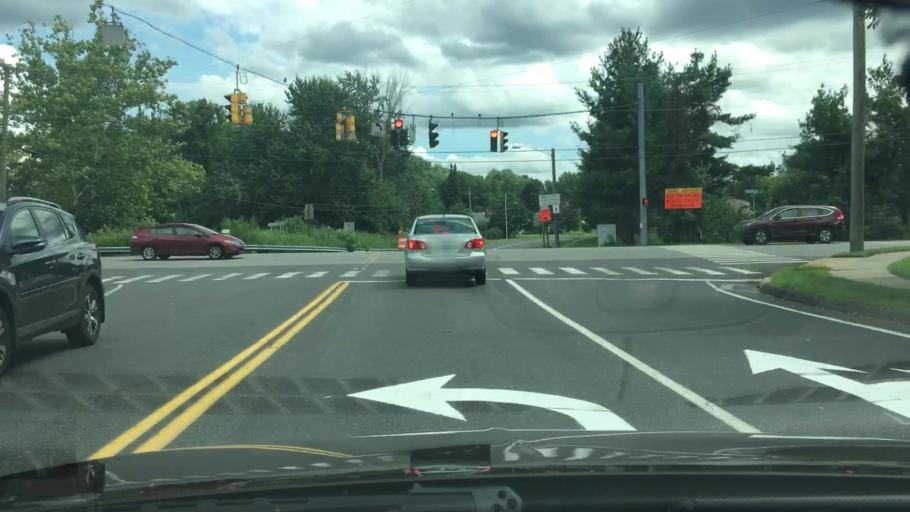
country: US
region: Connecticut
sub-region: Hartford County
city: Wethersfield
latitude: 41.6997
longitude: -72.6558
